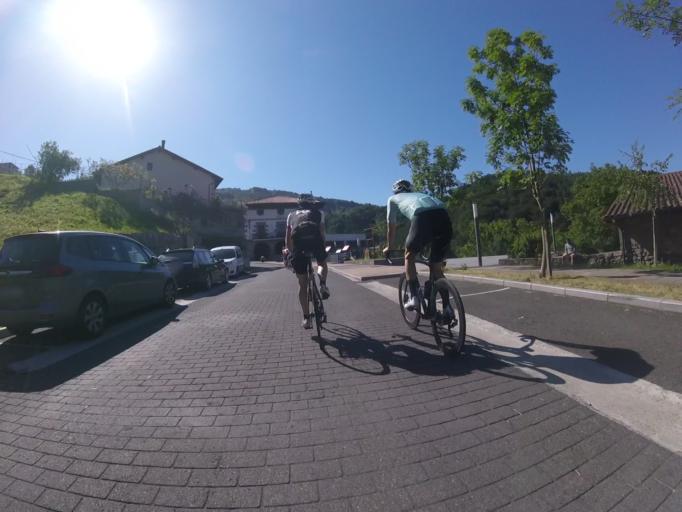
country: ES
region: Basque Country
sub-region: Provincia de Guipuzcoa
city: Beizama
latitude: 43.1345
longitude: -2.2007
